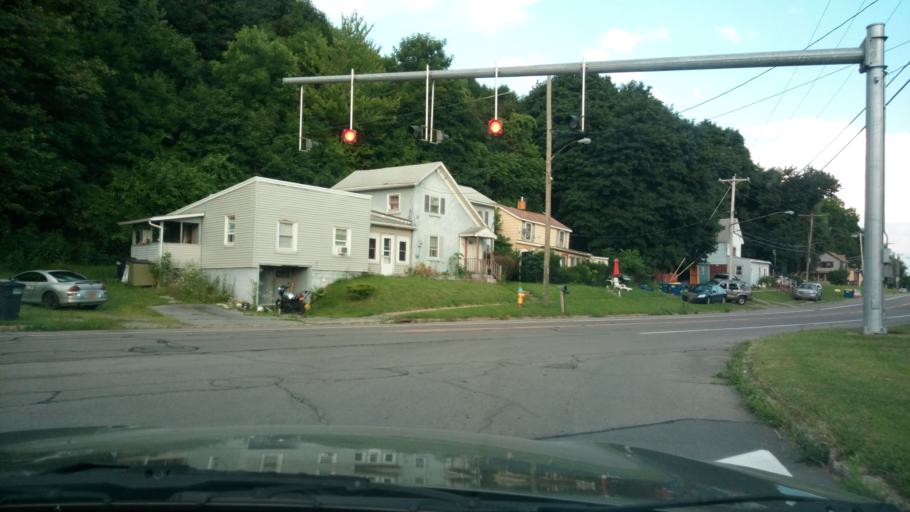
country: US
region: New York
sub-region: Wayne County
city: Clyde
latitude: 43.0823
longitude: -76.8670
